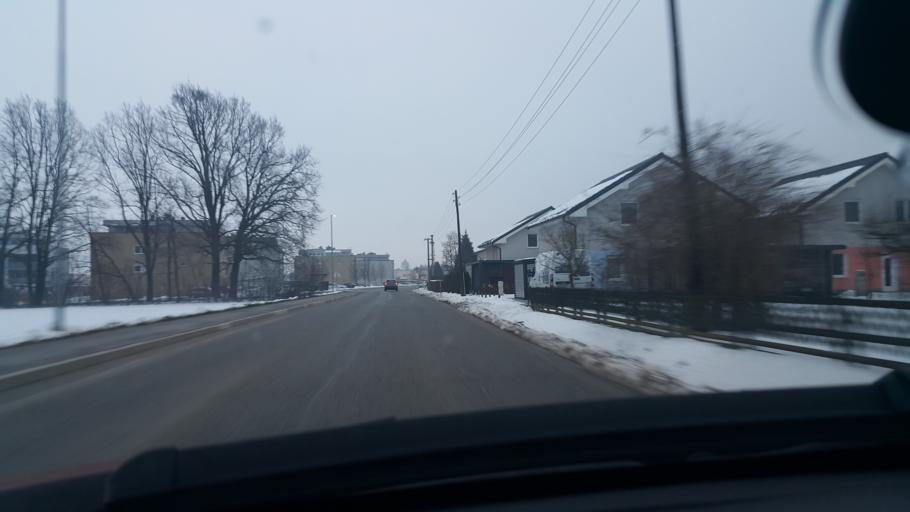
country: SI
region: Hoce-Slivnica
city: Hotinja Vas
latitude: 46.4591
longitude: 15.6736
